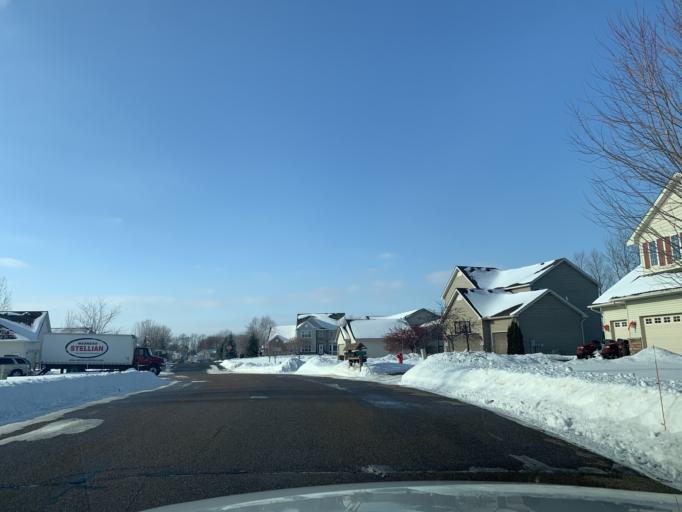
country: US
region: Minnesota
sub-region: Wright County
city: Buffalo
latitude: 45.2020
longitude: -93.8327
